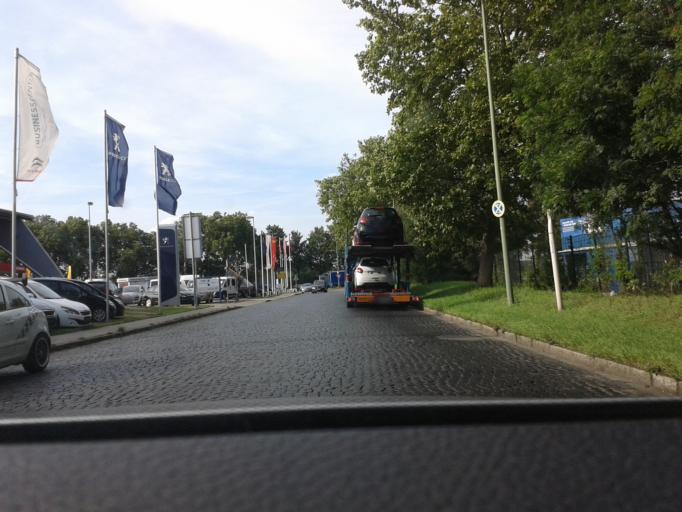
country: DE
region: North Rhine-Westphalia
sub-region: Regierungsbezirk Dusseldorf
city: Duisburg
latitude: 51.4426
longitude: 6.7619
